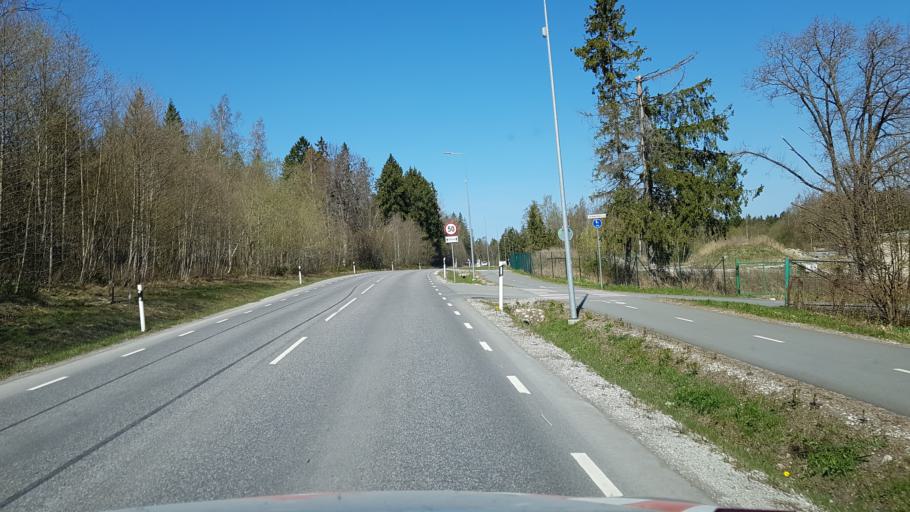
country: EE
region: Harju
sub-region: Viimsi vald
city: Viimsi
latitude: 59.5275
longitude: 24.8800
